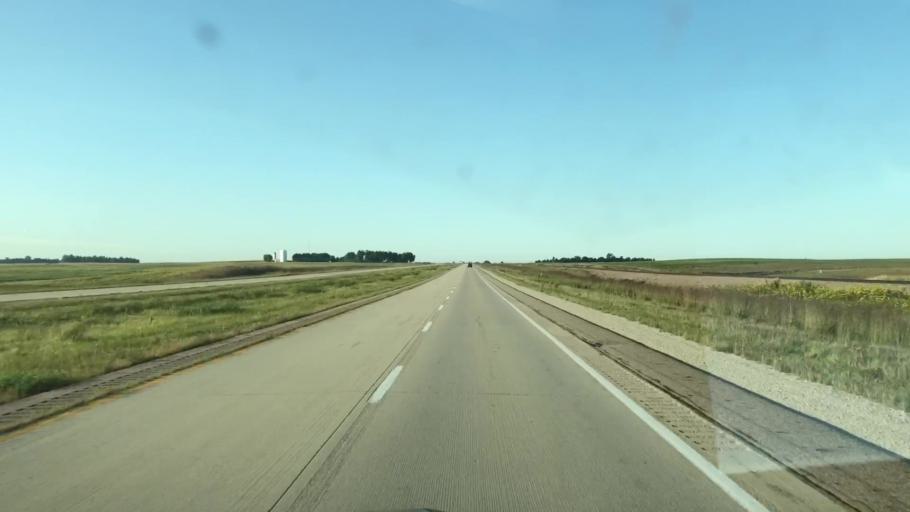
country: US
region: Iowa
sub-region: Osceola County
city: Sibley
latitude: 43.4753
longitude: -95.7065
